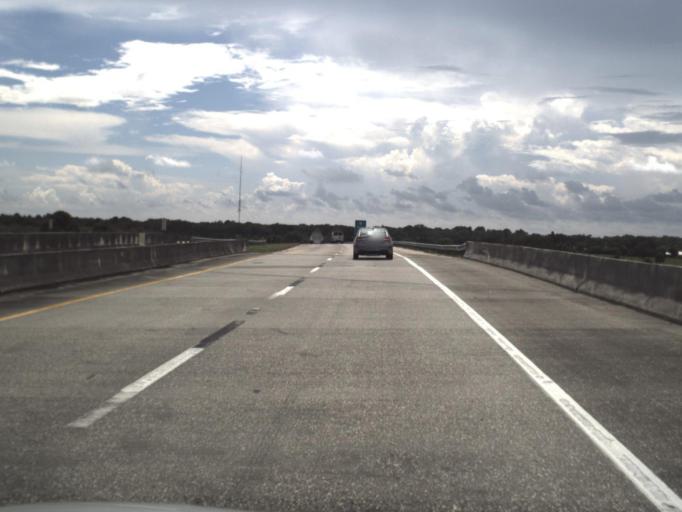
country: US
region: Florida
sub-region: Sarasota County
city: Laurel
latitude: 27.1683
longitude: -82.4562
